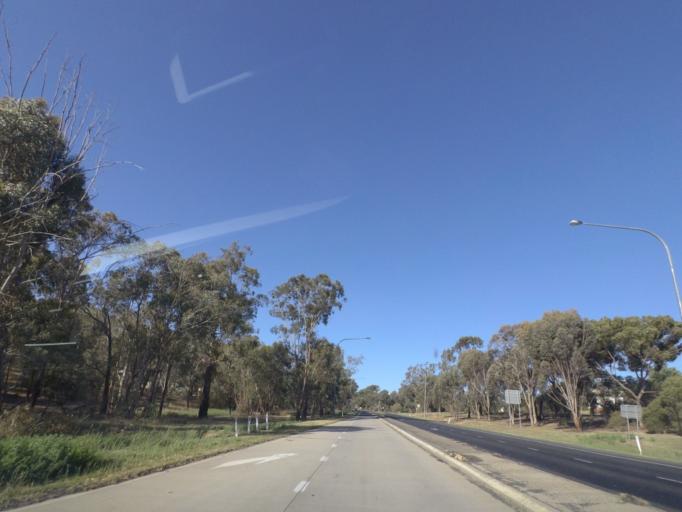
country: AU
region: New South Wales
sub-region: Wagga Wagga
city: Forest Hill
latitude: -35.2750
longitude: 147.7399
